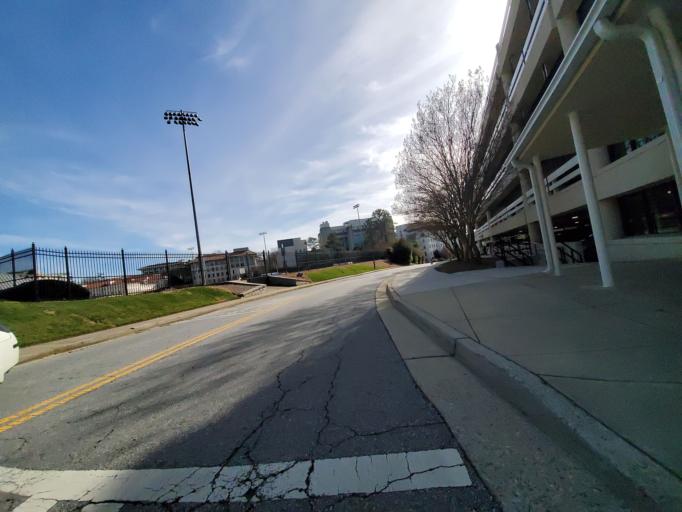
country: US
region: Georgia
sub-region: DeKalb County
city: Druid Hills
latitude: 33.7932
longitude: -84.3277
